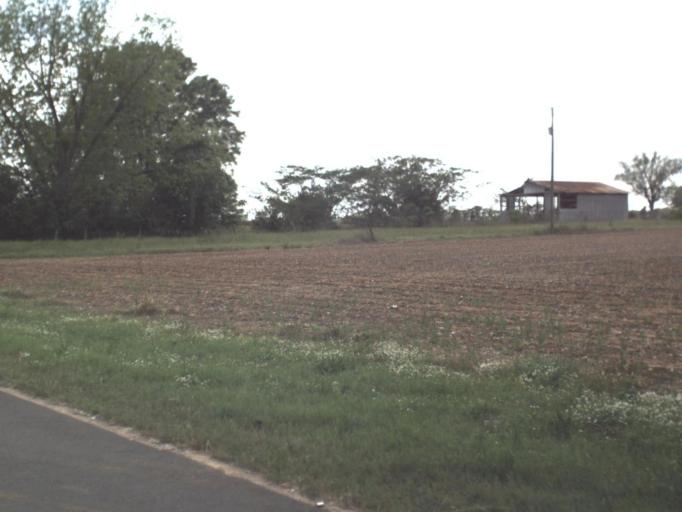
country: US
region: Florida
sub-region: Escambia County
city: Century
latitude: 30.9332
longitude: -87.1571
